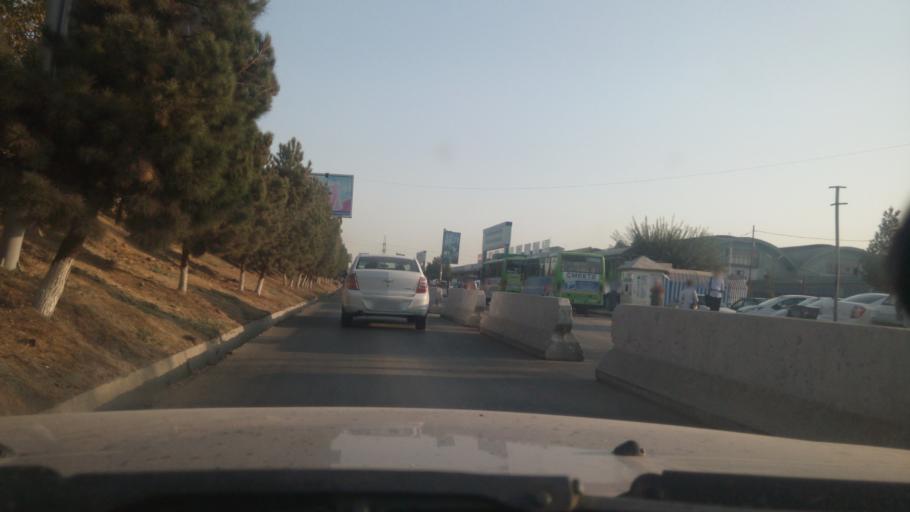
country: UZ
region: Toshkent Shahri
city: Tashkent
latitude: 41.2855
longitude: 69.1493
